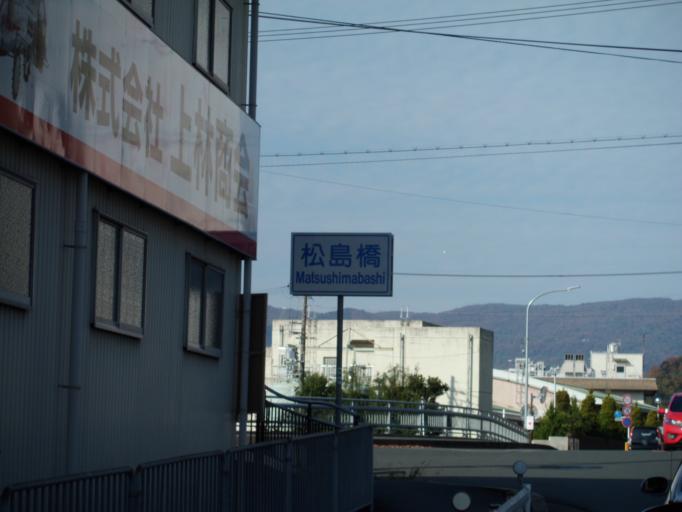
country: JP
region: Kyoto
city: Maizuru
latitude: 35.4776
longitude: 135.4010
